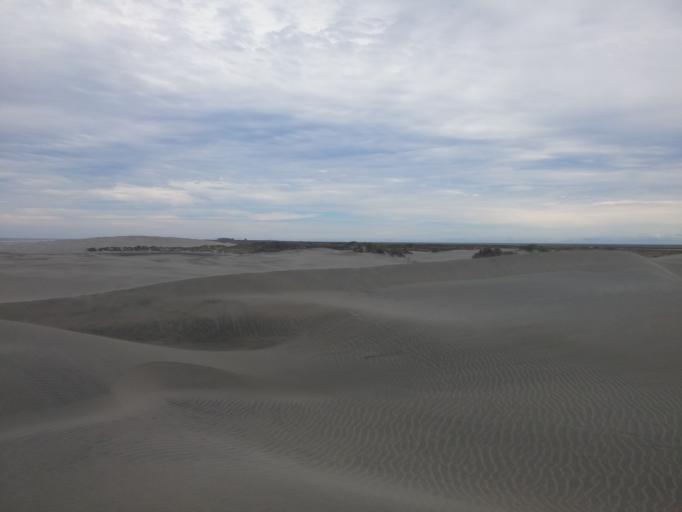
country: NZ
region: Tasman
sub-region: Tasman District
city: Takaka
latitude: -40.5199
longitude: 172.9308
